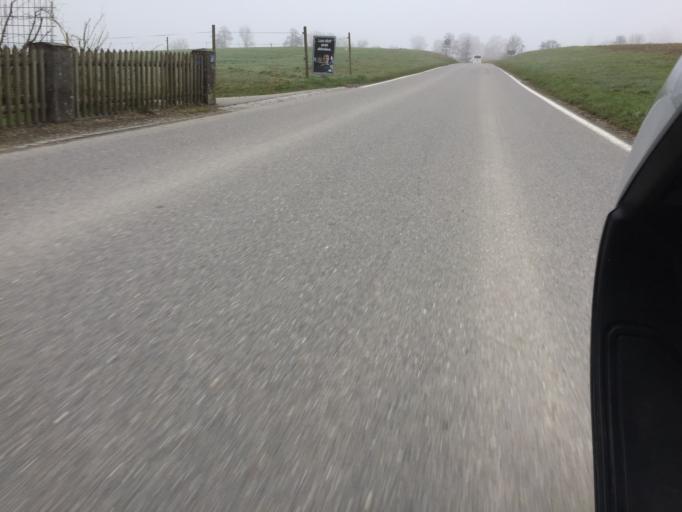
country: CH
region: Bern
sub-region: Seeland District
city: Grossaffoltern
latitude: 47.0851
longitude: 7.3791
